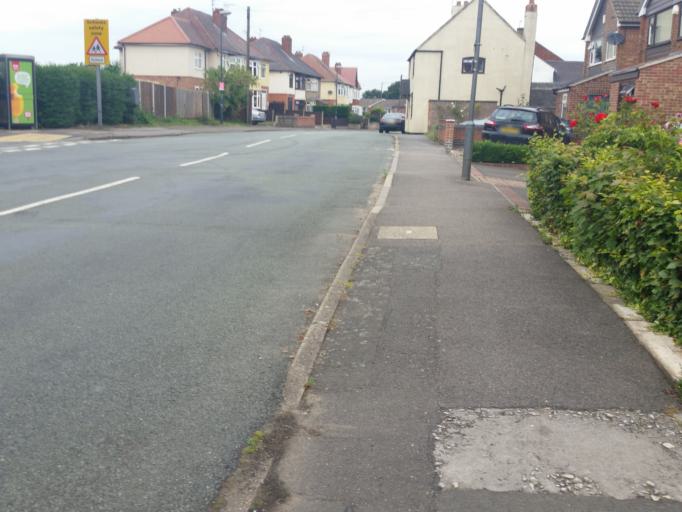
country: GB
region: England
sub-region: Derbyshire
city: Borrowash
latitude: 52.8977
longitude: -1.4216
